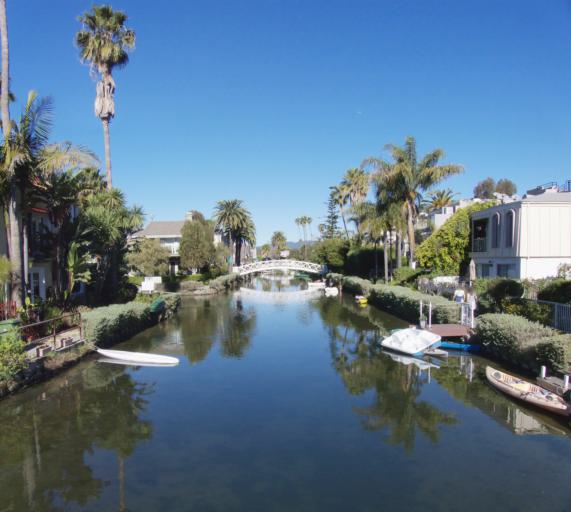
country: US
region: California
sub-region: Los Angeles County
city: Marina del Rey
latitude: 33.9856
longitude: -118.4647
